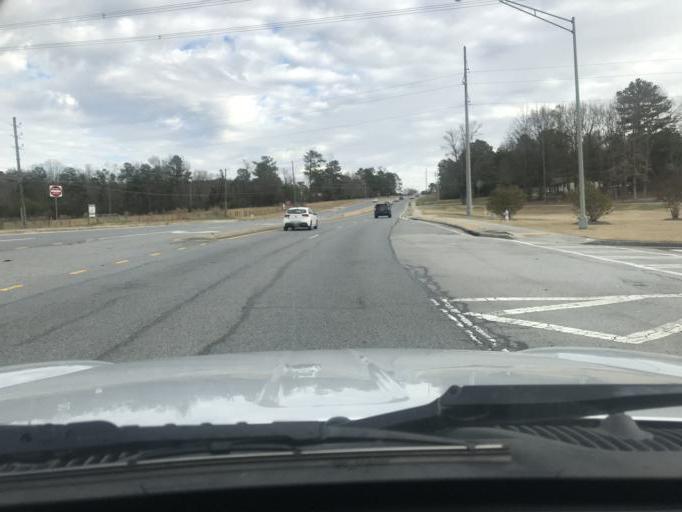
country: US
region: Georgia
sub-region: Gwinnett County
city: Buford
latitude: 34.0703
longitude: -83.9614
